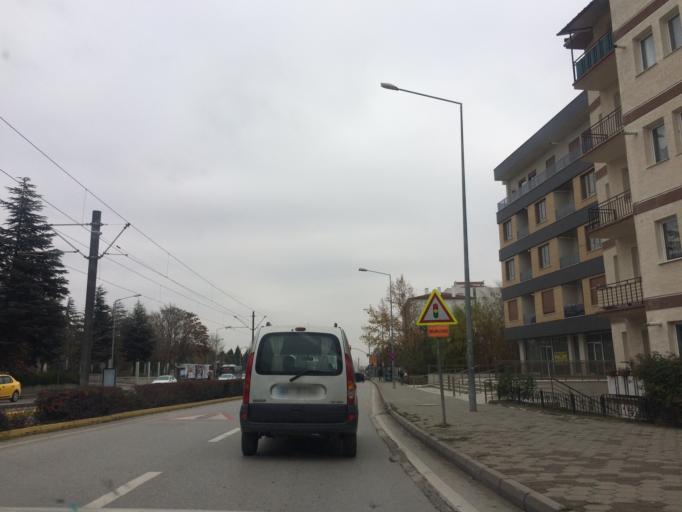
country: TR
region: Eskisehir
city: Eskisehir
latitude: 39.7895
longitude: 30.4911
